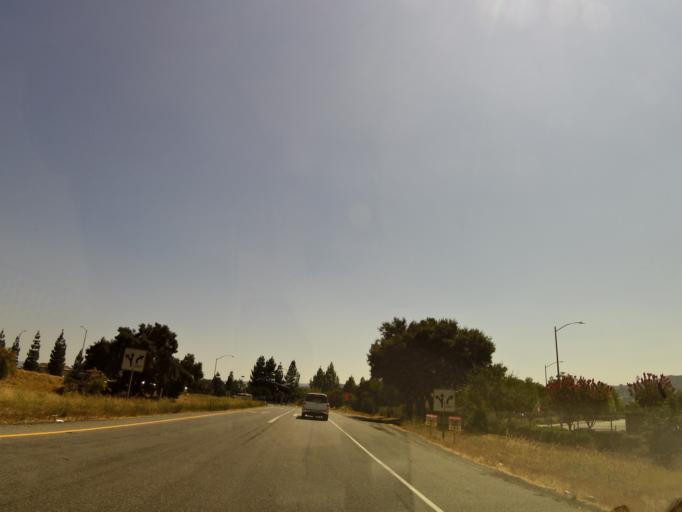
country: US
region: California
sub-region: Santa Clara County
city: Morgan Hill
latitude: 37.1320
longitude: -121.6352
